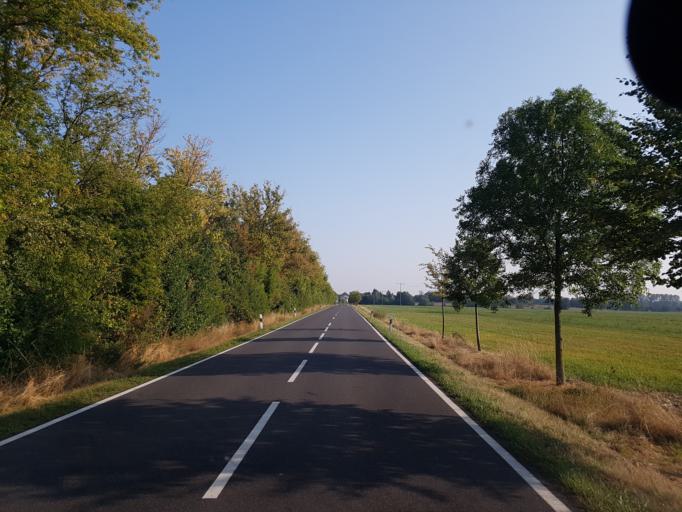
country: DE
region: Brandenburg
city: Finsterwalde
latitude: 51.6583
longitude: 13.7350
